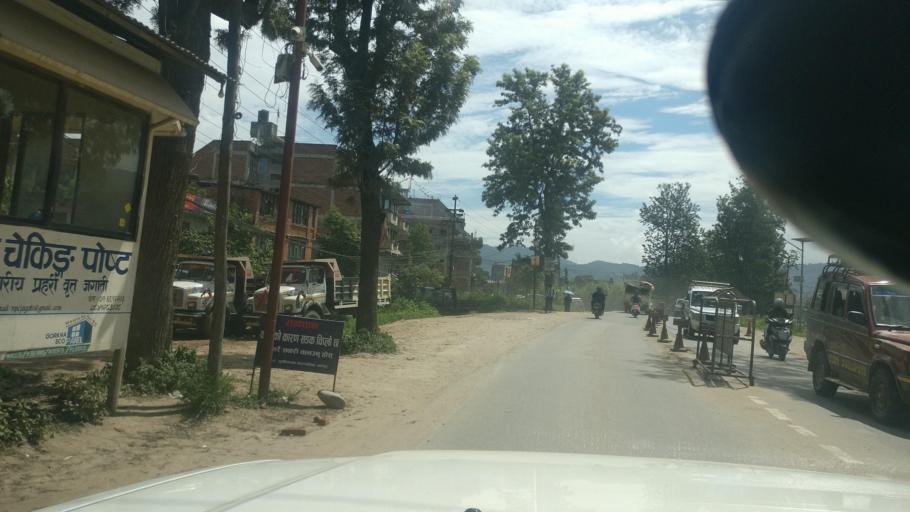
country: NP
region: Central Region
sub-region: Bagmati Zone
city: Bhaktapur
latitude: 27.6659
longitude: 85.4389
